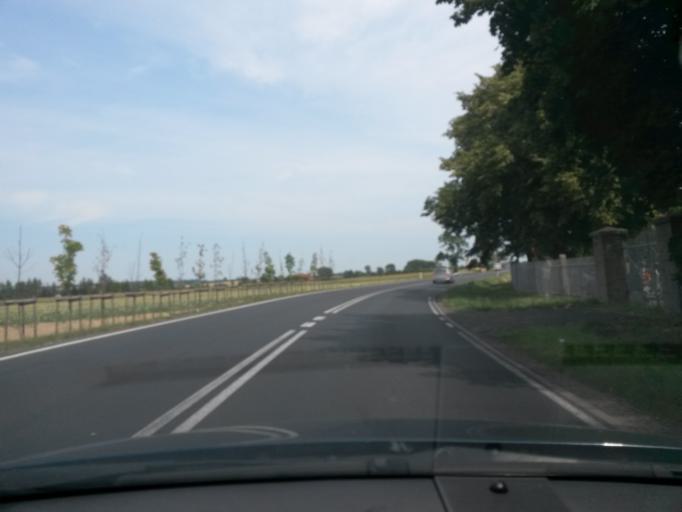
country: PL
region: Greater Poland Voivodeship
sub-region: Powiat gostynski
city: Gostyn
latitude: 51.9364
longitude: 17.0189
